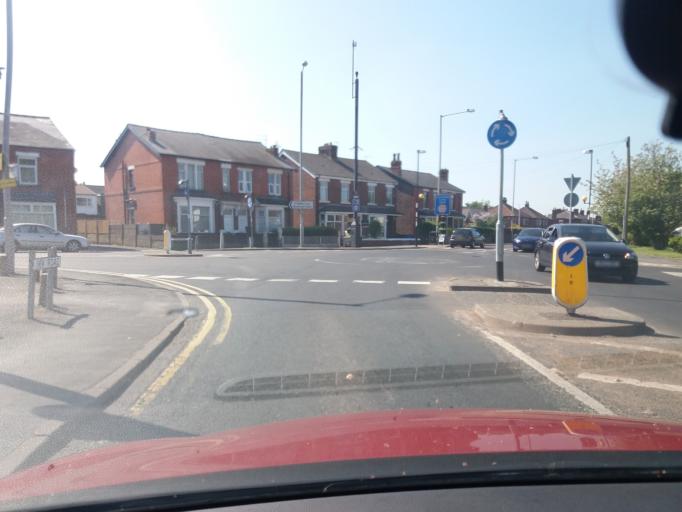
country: GB
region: England
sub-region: Lancashire
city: Coppull
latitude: 53.6273
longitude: -2.6563
